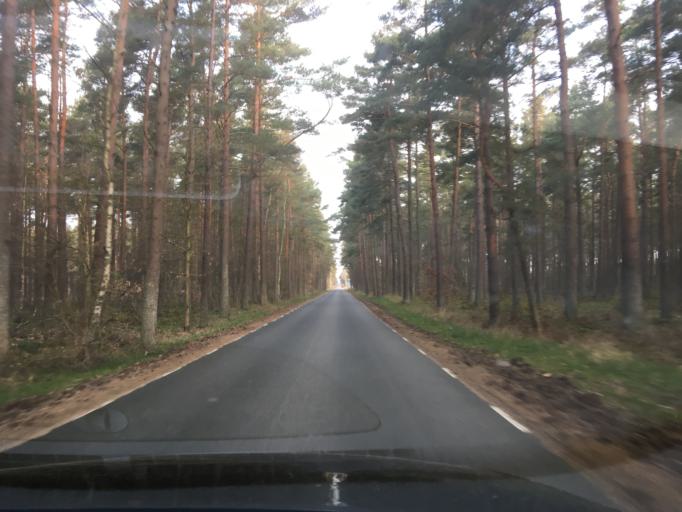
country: SE
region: Skane
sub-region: Simrishamns Kommun
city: Simrishamn
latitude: 55.3917
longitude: 14.1853
